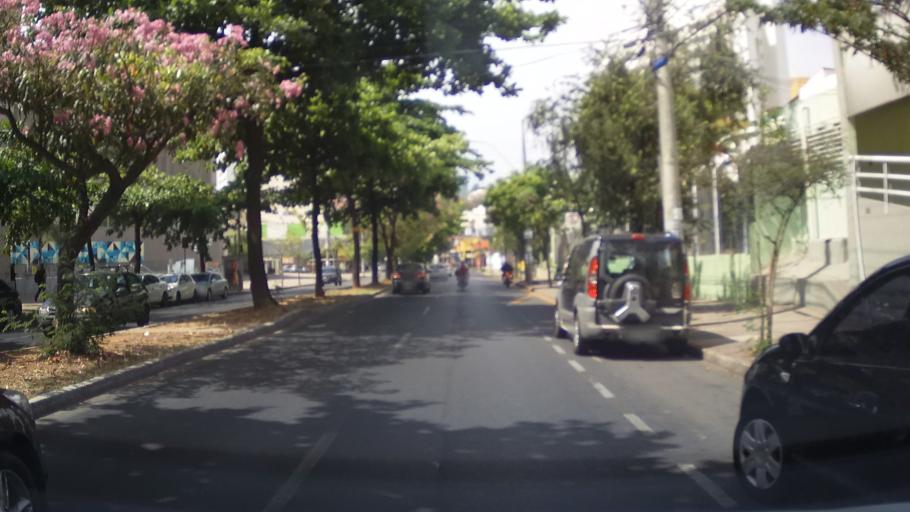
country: BR
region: Minas Gerais
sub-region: Belo Horizonte
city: Belo Horizonte
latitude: -19.9365
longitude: -43.9724
